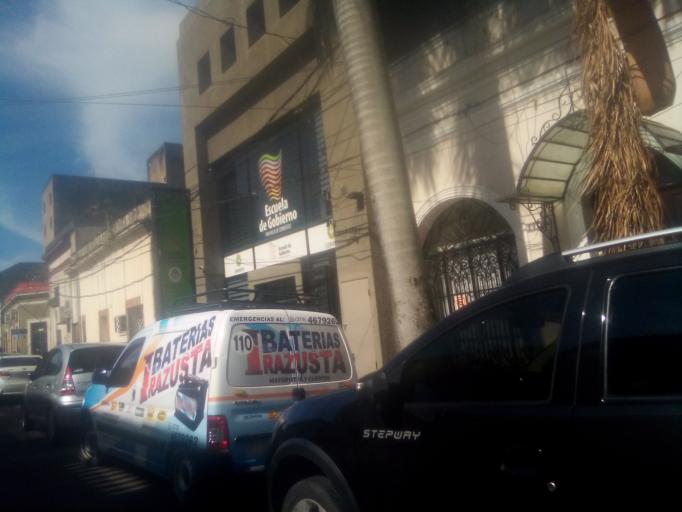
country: AR
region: Corrientes
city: Corrientes
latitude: -27.4665
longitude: -58.8405
